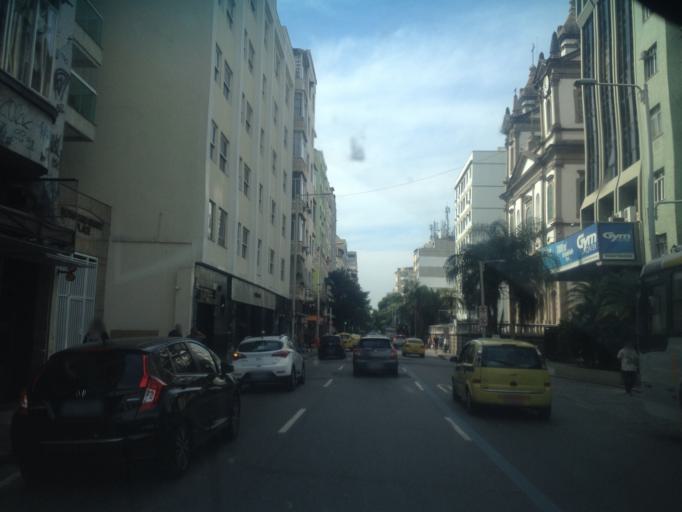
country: BR
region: Rio de Janeiro
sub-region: Rio De Janeiro
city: Rio de Janeiro
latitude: -22.9541
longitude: -43.1920
